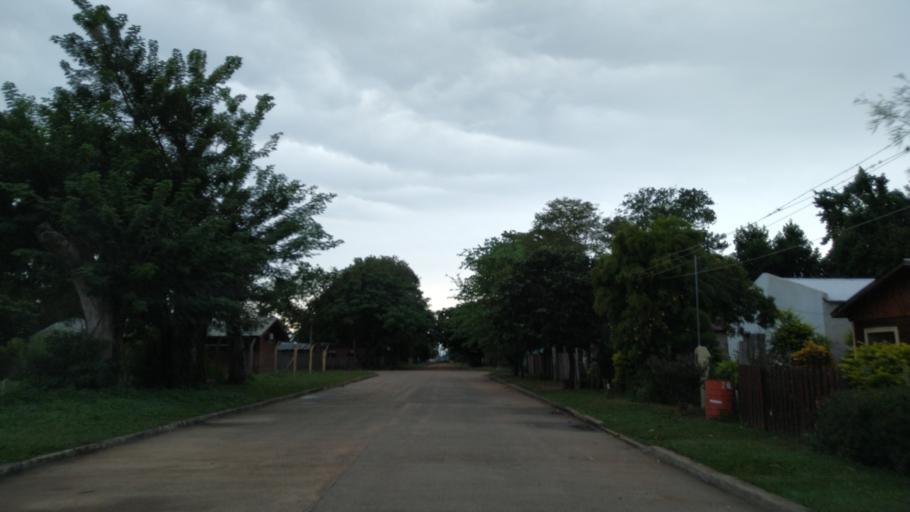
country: AR
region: Corrientes
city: Ituzaingo
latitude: -27.6330
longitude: -56.9054
